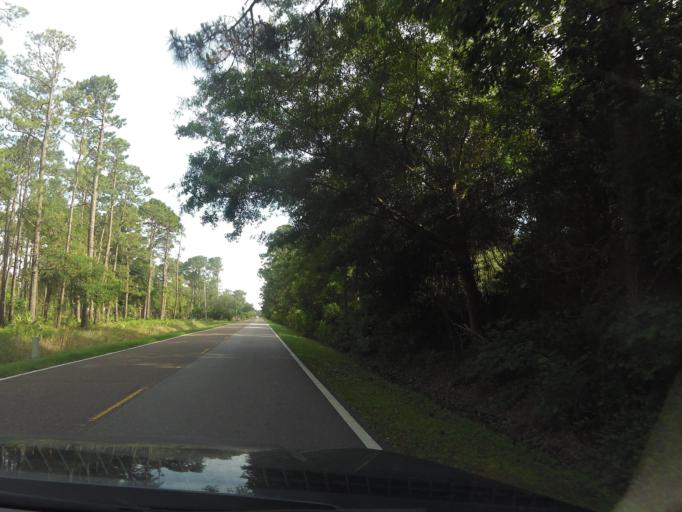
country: US
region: Florida
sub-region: Duval County
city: Atlantic Beach
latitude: 30.4859
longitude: -81.4719
